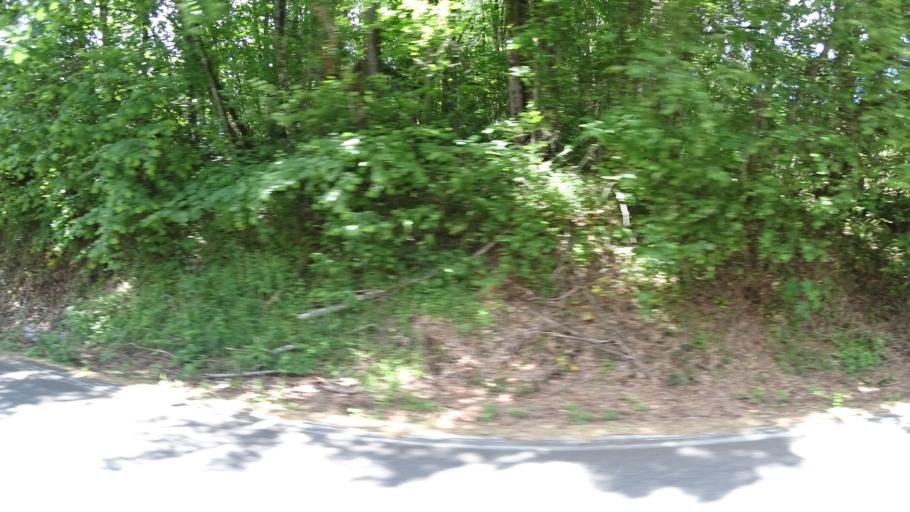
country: US
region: Oregon
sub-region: Washington County
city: Bethany
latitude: 45.6038
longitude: -122.8297
